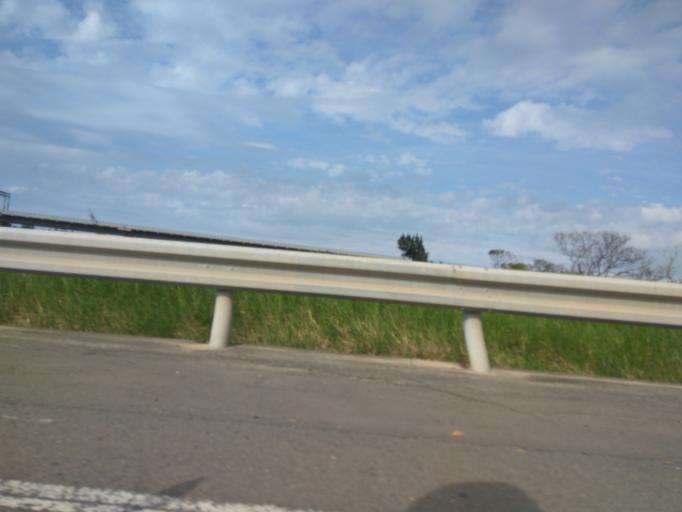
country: TW
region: Taiwan
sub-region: Hsinchu
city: Zhubei
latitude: 24.9657
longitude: 121.0162
